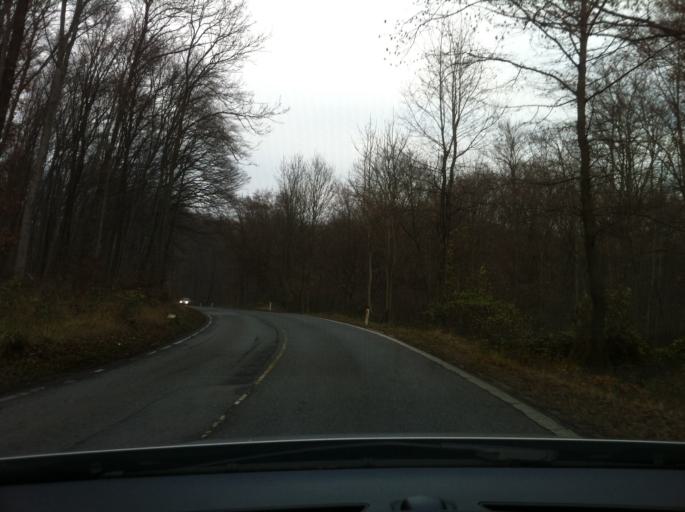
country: AT
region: Lower Austria
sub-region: Politischer Bezirk Wien-Umgebung
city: Purkersdorf
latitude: 48.2267
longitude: 16.2555
